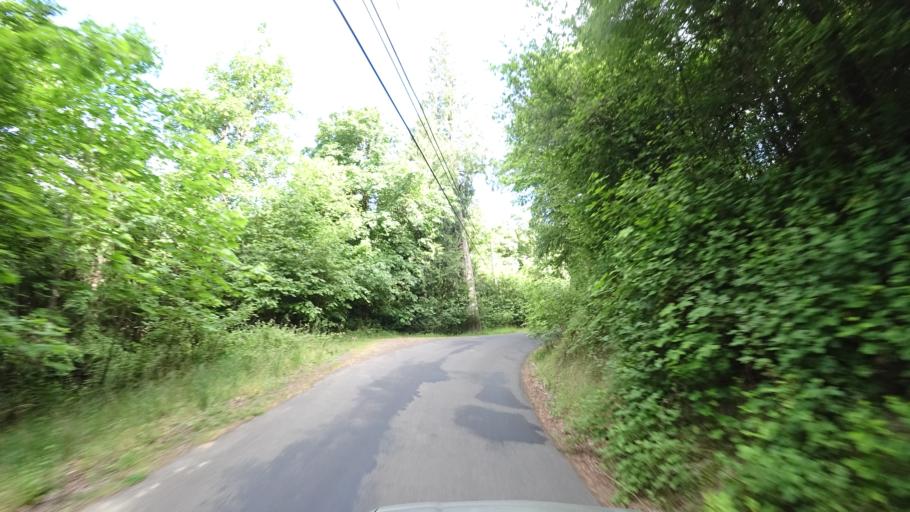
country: US
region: Oregon
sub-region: Washington County
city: Oak Hills
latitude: 45.5793
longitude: -122.8116
